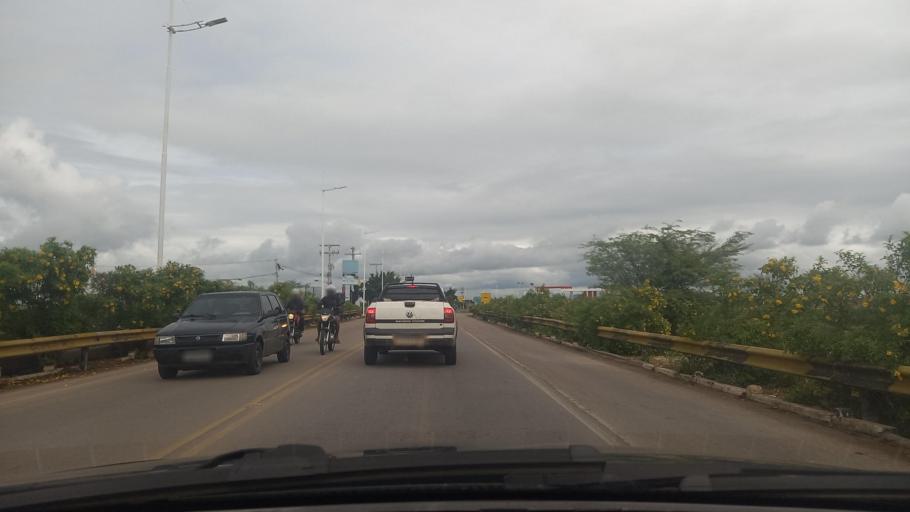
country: BR
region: Bahia
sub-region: Paulo Afonso
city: Paulo Afonso
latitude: -9.4309
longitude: -38.2276
